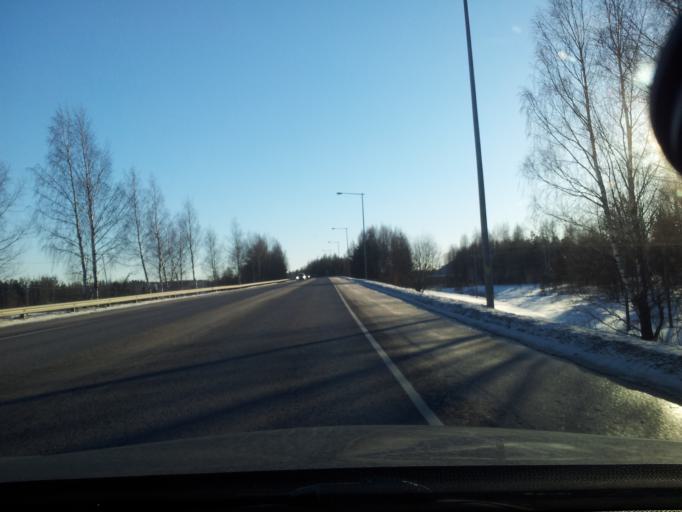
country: FI
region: Uusimaa
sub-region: Helsinki
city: Vihti
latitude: 60.3420
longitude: 24.3326
